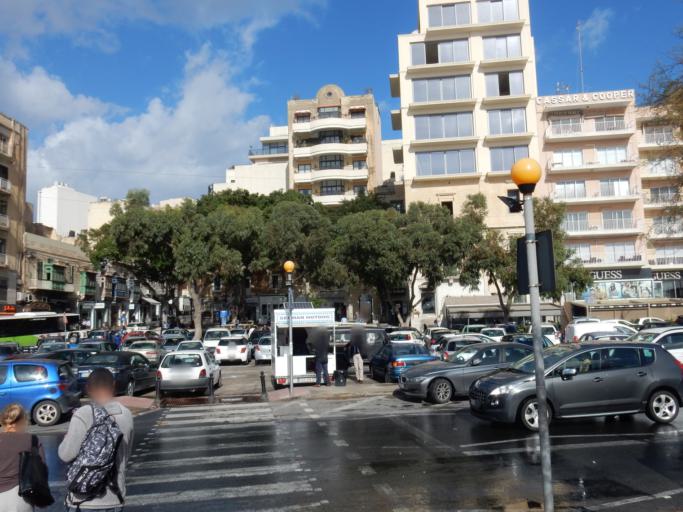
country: MT
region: Tas-Sliema
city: Sliema
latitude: 35.9087
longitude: 14.5053
